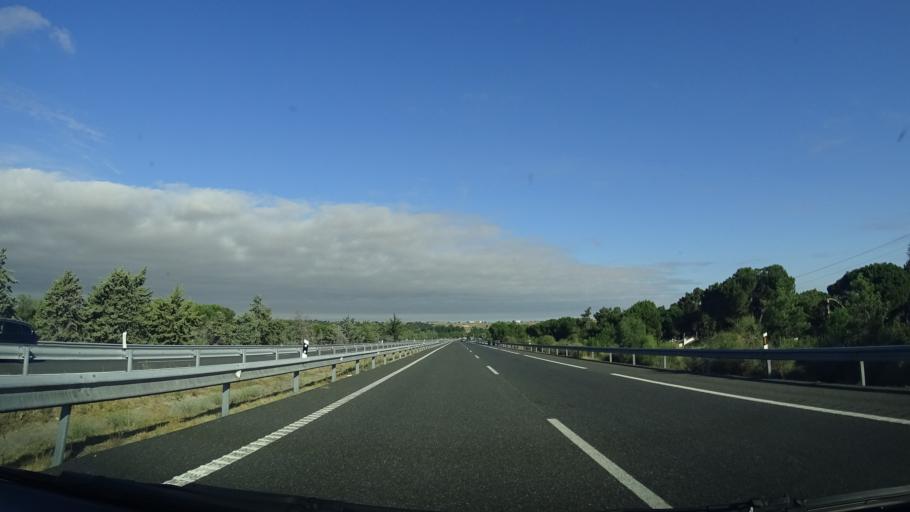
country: ES
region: Castille and Leon
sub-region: Provincia de Segovia
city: Labajos
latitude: 40.8593
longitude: -4.5547
